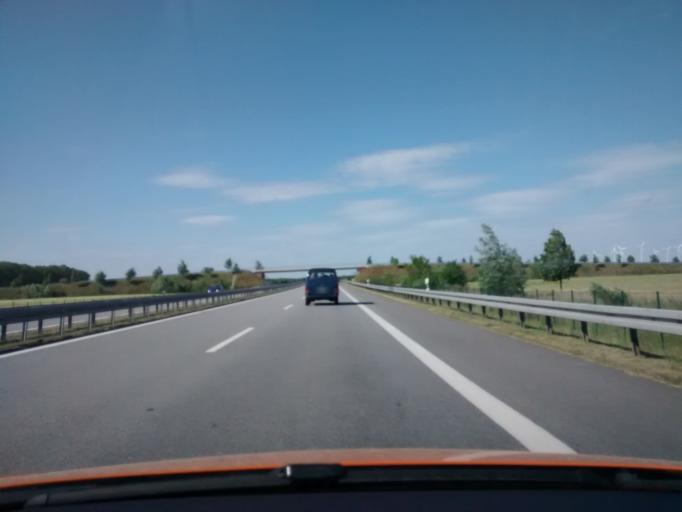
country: DE
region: Brandenburg
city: Trebbin
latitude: 52.1747
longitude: 13.2455
